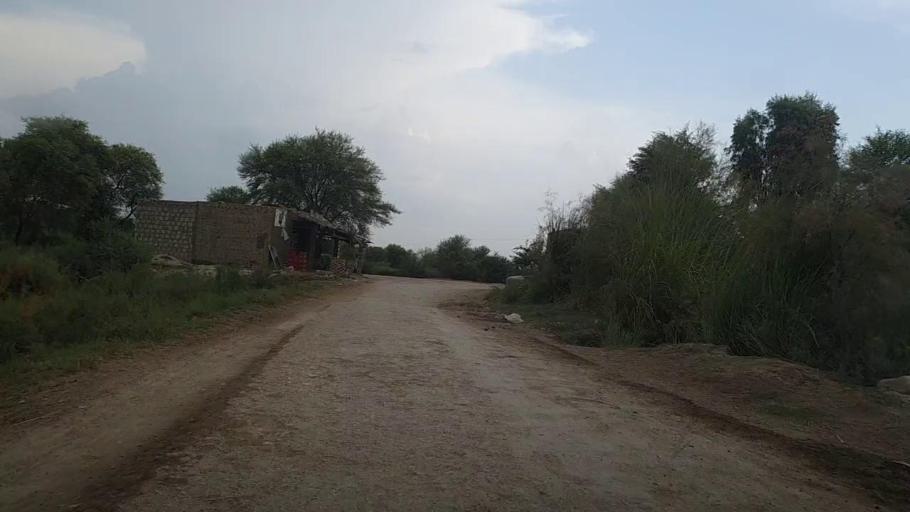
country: PK
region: Sindh
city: Khanpur
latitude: 27.8391
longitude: 69.4847
